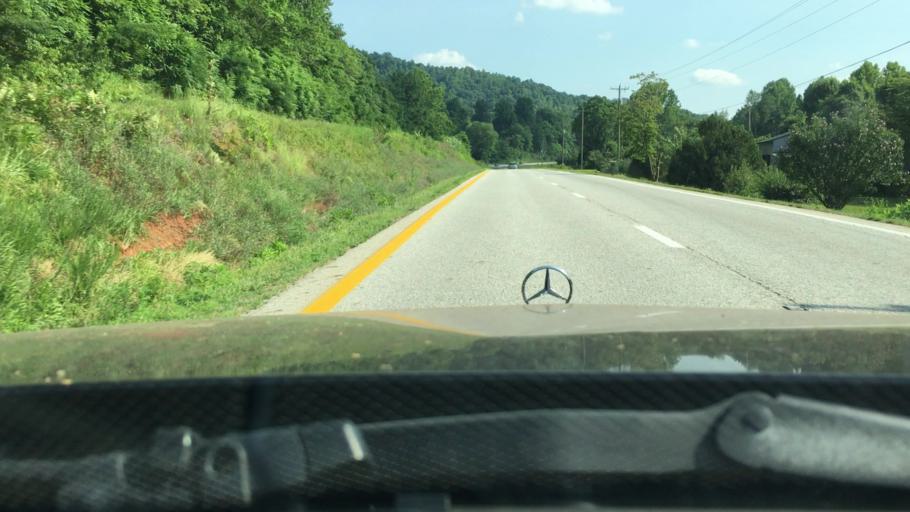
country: US
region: Virginia
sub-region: Nelson County
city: Lovingston
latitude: 37.8009
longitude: -78.8622
